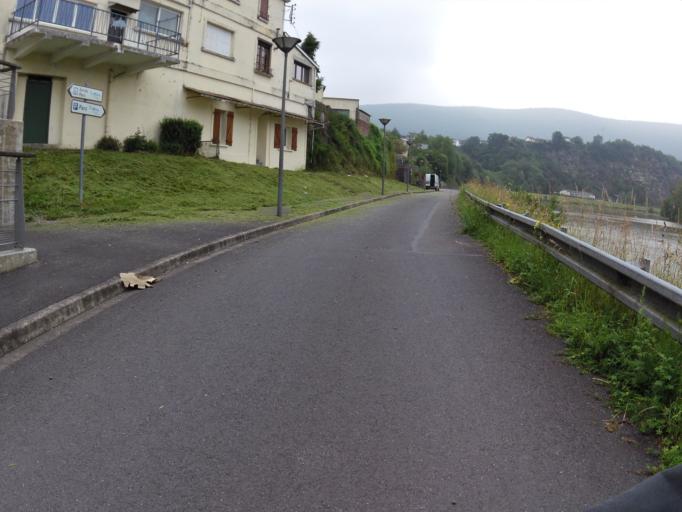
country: FR
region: Champagne-Ardenne
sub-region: Departement des Ardennes
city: Fumay
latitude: 49.9897
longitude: 4.6990
